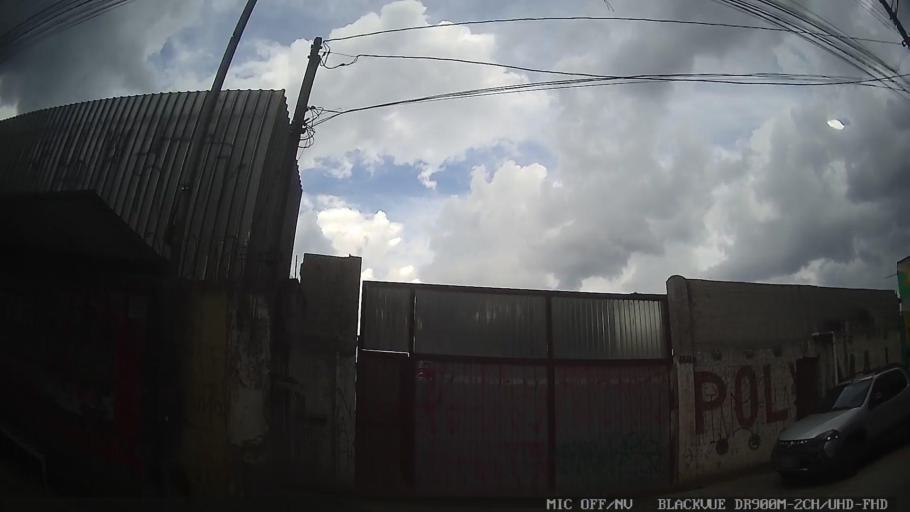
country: BR
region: Sao Paulo
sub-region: Ribeirao Pires
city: Ribeirao Pires
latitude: -23.6750
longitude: -46.4210
